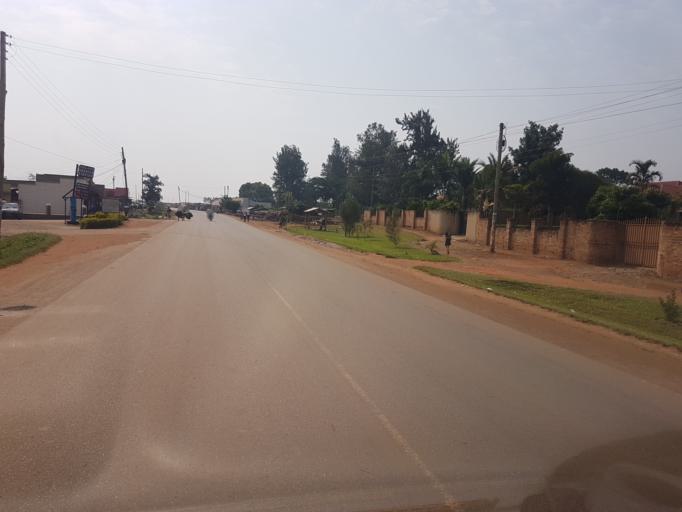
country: UG
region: Western Region
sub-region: Mbarara District
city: Mbarara
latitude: -0.6350
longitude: 30.6172
